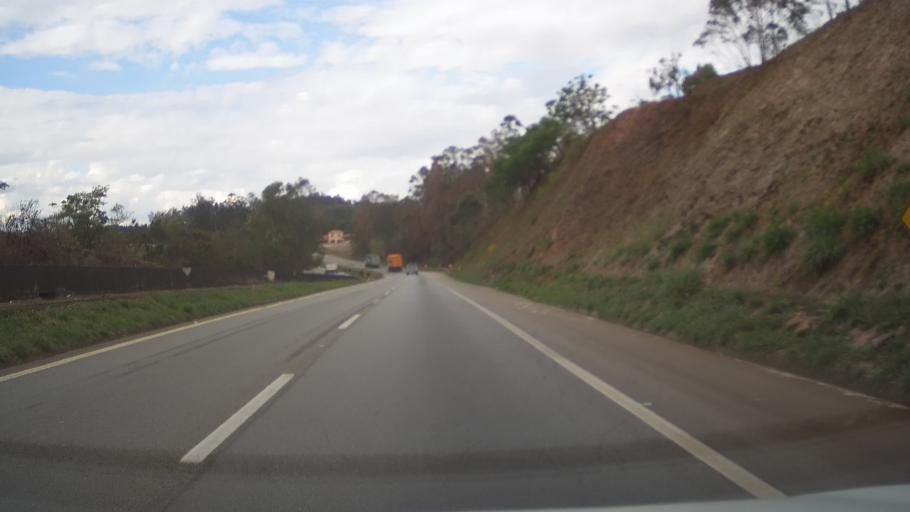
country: BR
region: Minas Gerais
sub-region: Itauna
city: Itauna
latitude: -20.2975
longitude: -44.4395
